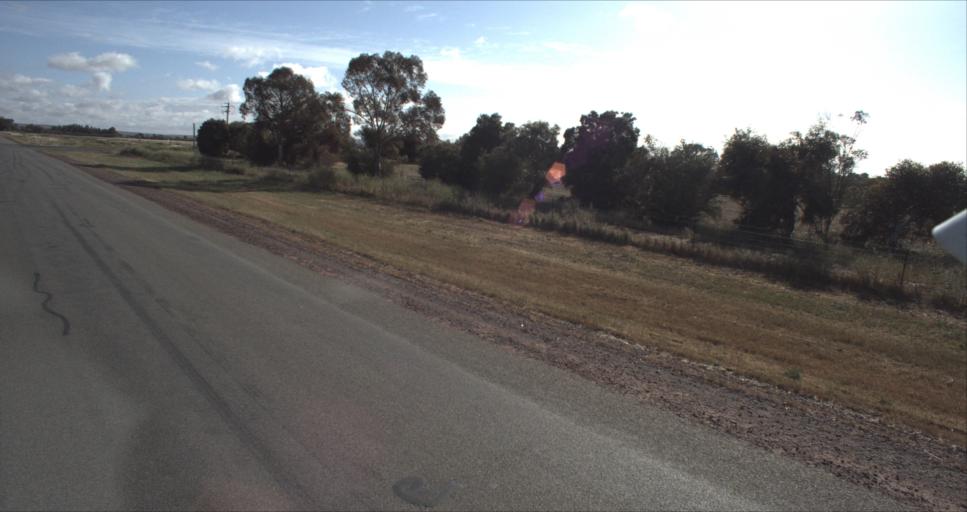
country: AU
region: New South Wales
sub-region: Leeton
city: Leeton
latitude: -34.5276
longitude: 146.3894
